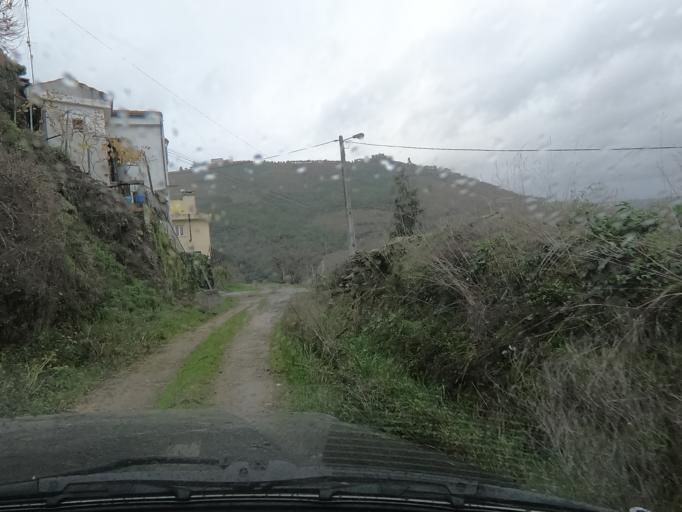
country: PT
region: Vila Real
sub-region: Santa Marta de Penaguiao
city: Santa Marta de Penaguiao
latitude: 41.2233
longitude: -7.7507
